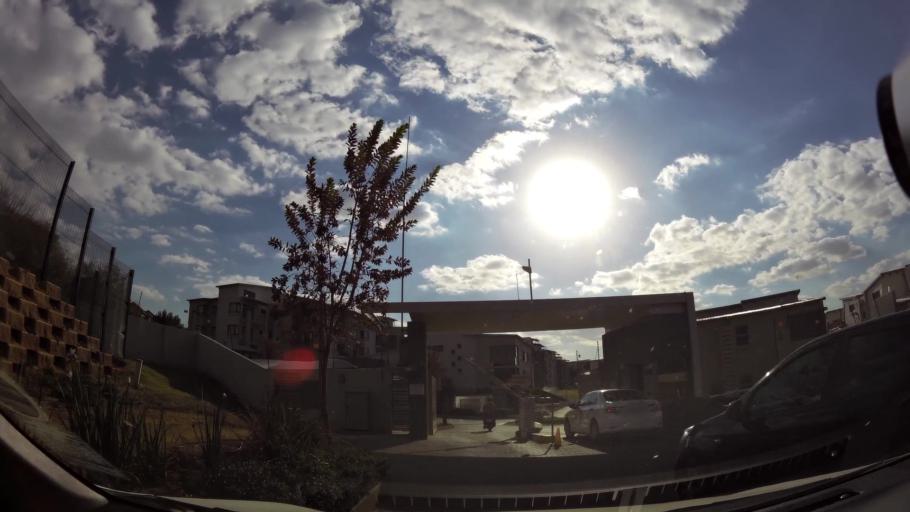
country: ZA
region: Gauteng
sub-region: City of Johannesburg Metropolitan Municipality
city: Diepsloot
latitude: -25.9987
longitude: 28.0175
